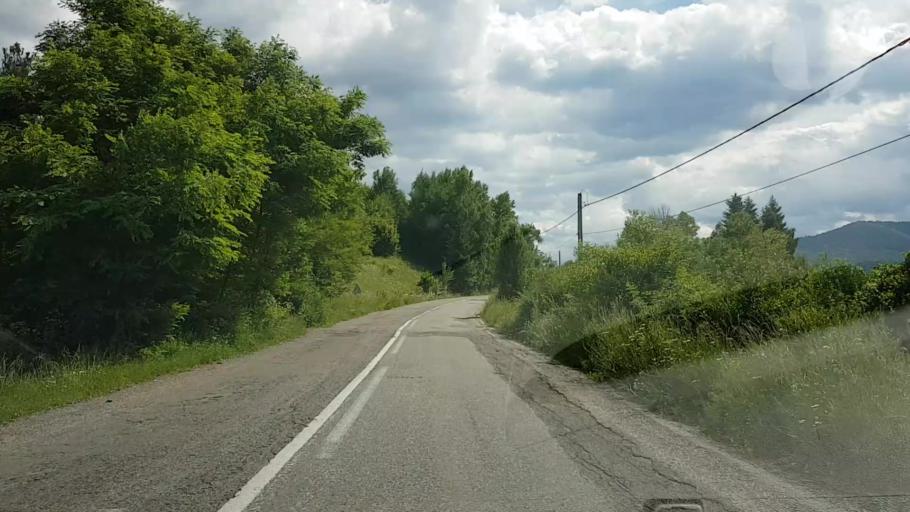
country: RO
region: Neamt
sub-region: Comuna Ceahlau
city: Ceahlau
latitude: 47.0722
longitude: 25.9620
